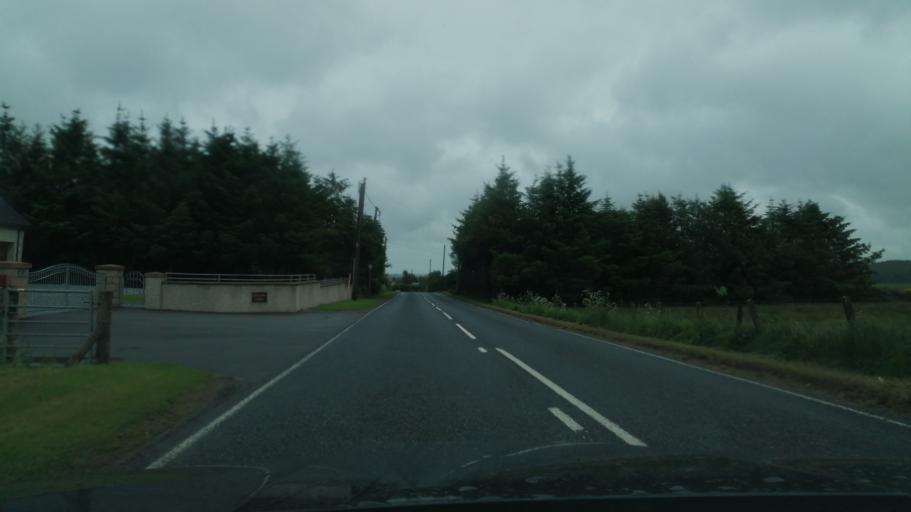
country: GB
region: Scotland
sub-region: Aberdeenshire
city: Portsoy
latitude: 57.5932
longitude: -2.7346
